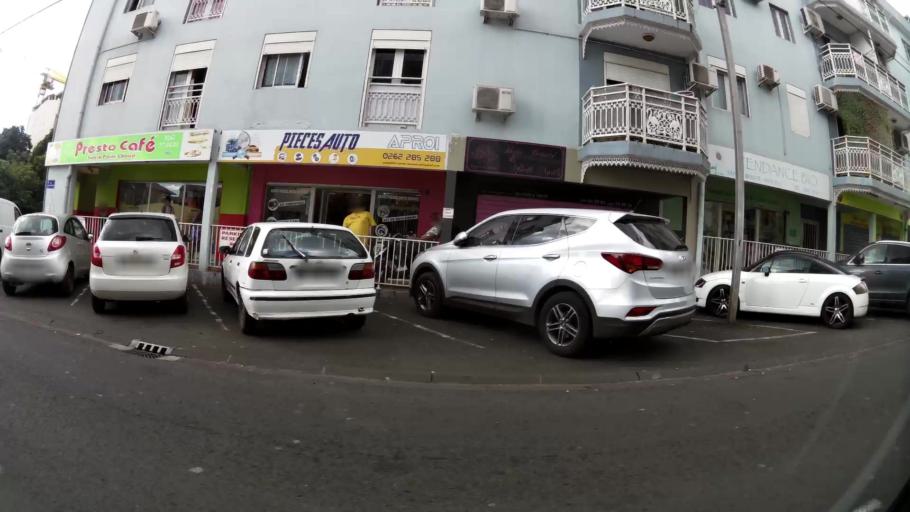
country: RE
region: Reunion
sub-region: Reunion
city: Saint-Denis
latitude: -20.8929
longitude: 55.4819
